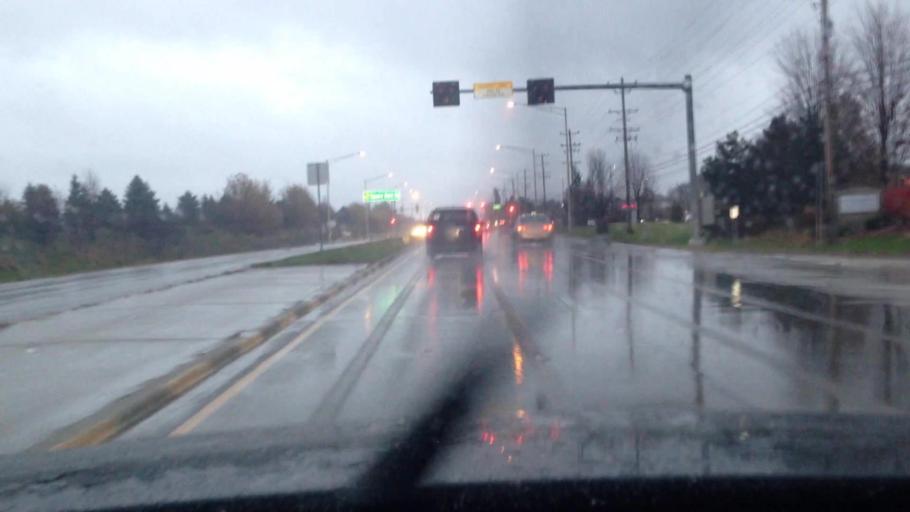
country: US
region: Illinois
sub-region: McHenry County
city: Lake in the Hills
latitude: 42.1757
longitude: -88.3720
